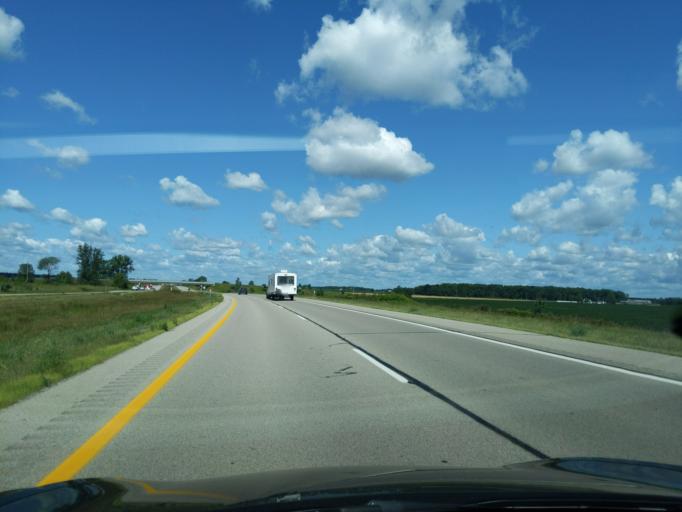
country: US
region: Michigan
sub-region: Isabella County
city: Shepherd
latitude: 43.5422
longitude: -84.6828
